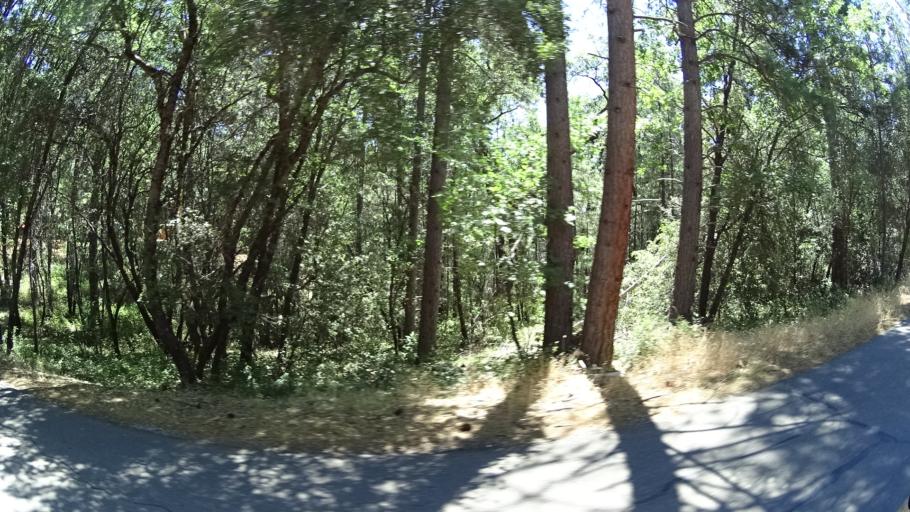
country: US
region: California
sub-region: Amador County
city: Pioneer
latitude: 38.3765
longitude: -120.5186
